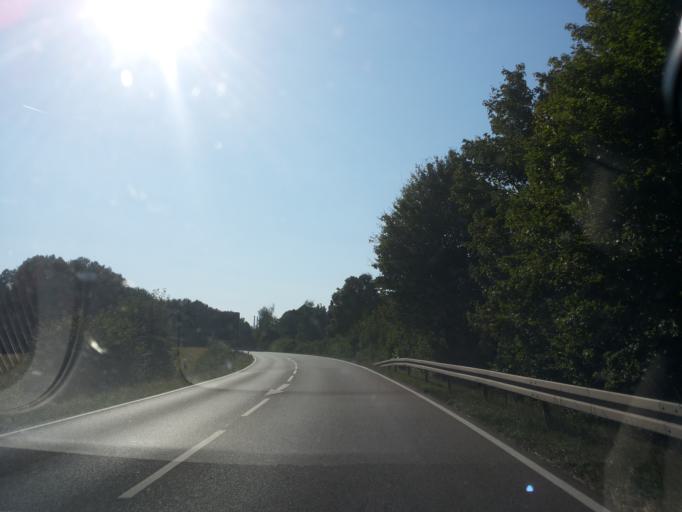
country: DE
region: Bavaria
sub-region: Upper Bavaria
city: Vohburg an der Donau
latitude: 48.7748
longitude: 11.6280
